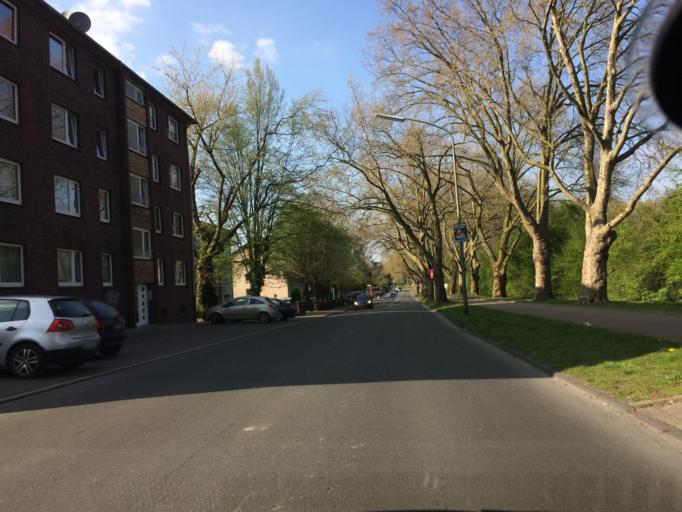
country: DE
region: North Rhine-Westphalia
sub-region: Regierungsbezirk Munster
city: Gelsenkirchen
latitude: 51.5213
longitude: 7.1065
